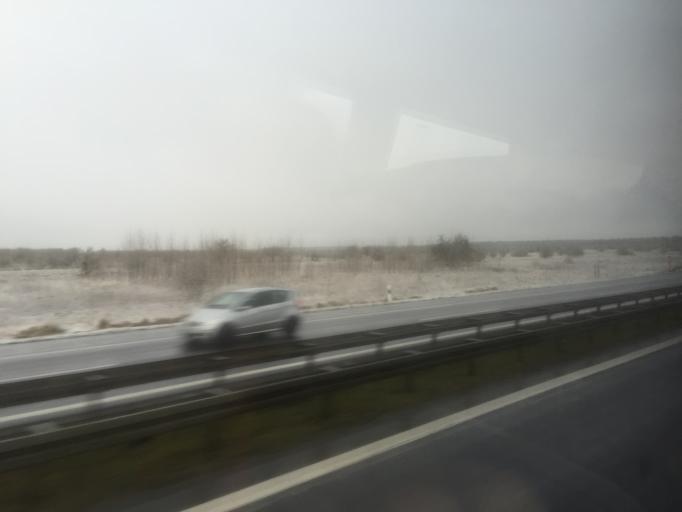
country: DE
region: Brandenburg
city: Mittenwalde
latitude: 52.3074
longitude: 13.5559
